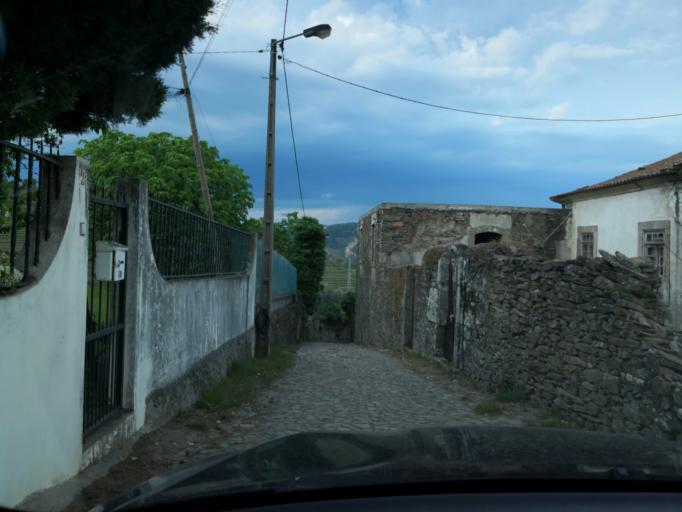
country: PT
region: Vila Real
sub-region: Sabrosa
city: Vilela
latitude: 41.2045
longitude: -7.6577
